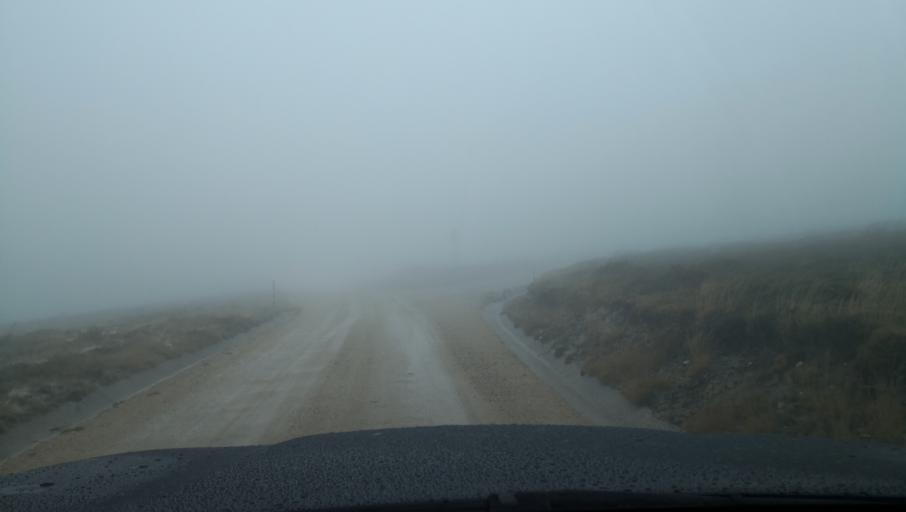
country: PT
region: Vila Real
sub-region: Vila Real
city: Vila Real
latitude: 41.3328
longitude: -7.8367
